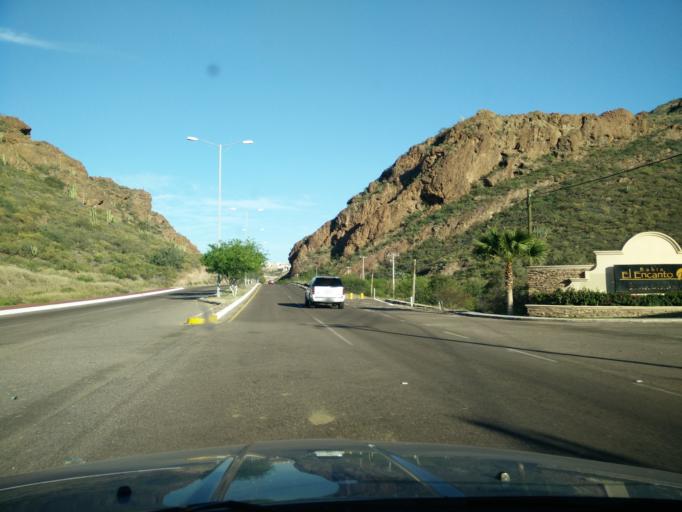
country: MX
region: Sonora
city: Heroica Guaymas
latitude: 27.9505
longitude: -111.0730
